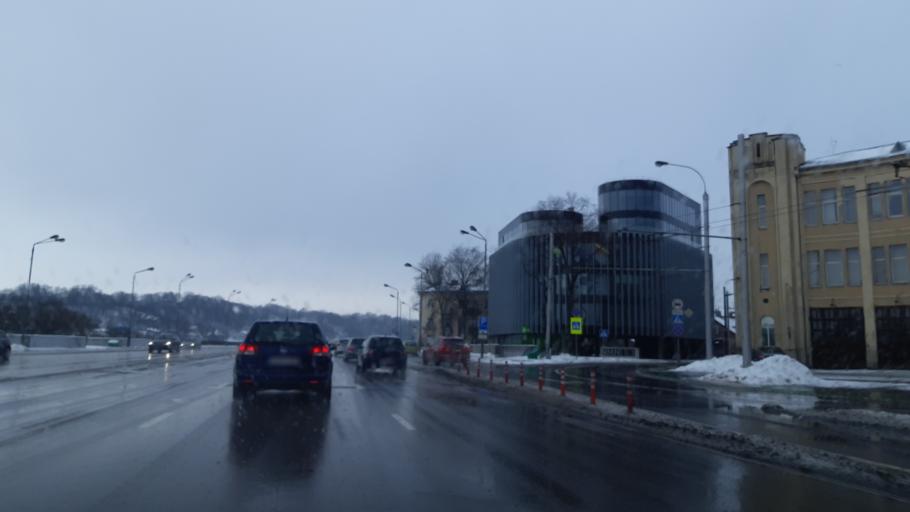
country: LT
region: Kauno apskritis
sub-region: Kaunas
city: Kaunas
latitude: 54.8946
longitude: 23.9031
